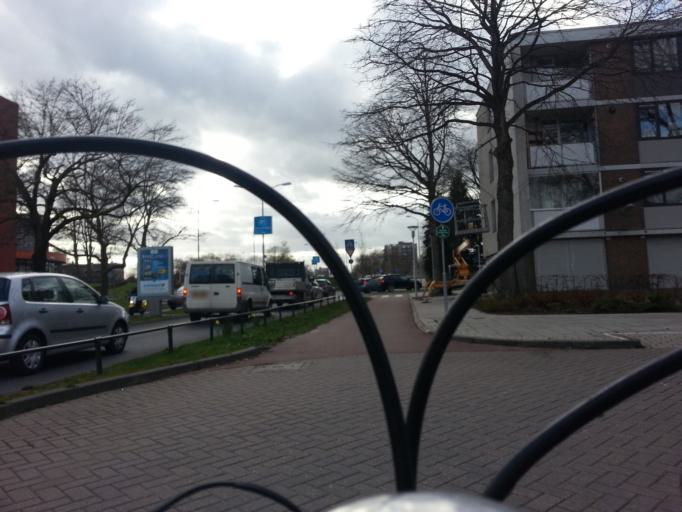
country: NL
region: North Brabant
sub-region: Gemeente Eindhoven
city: Villapark
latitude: 51.4575
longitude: 5.4889
